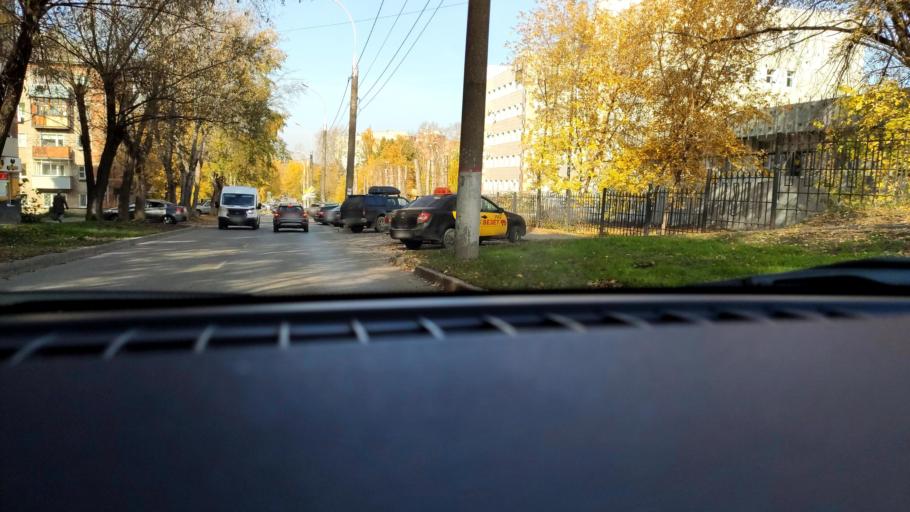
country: RU
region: Perm
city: Perm
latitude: 57.9833
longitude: 56.1905
